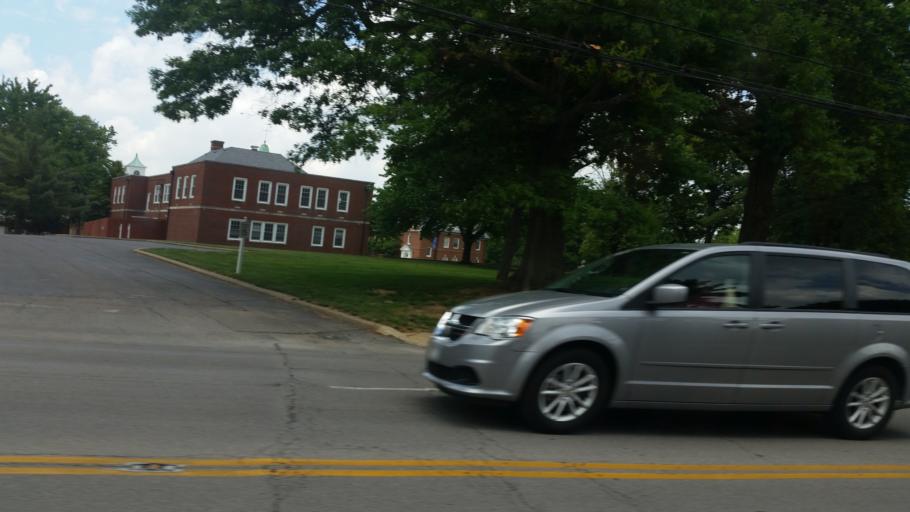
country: US
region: Kentucky
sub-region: Jefferson County
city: Saint Matthews
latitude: 38.2451
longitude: -85.6885
